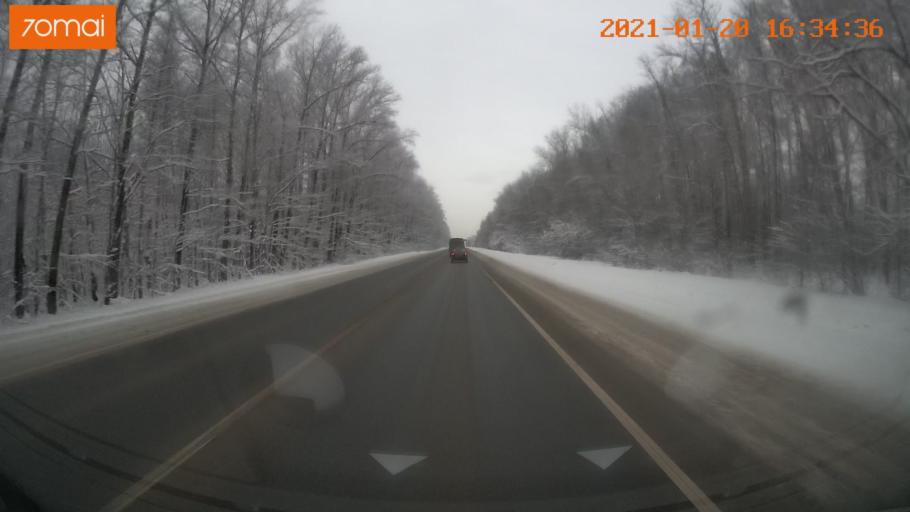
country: RU
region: Vladimir
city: Orgtrud
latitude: 56.2023
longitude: 40.7727
